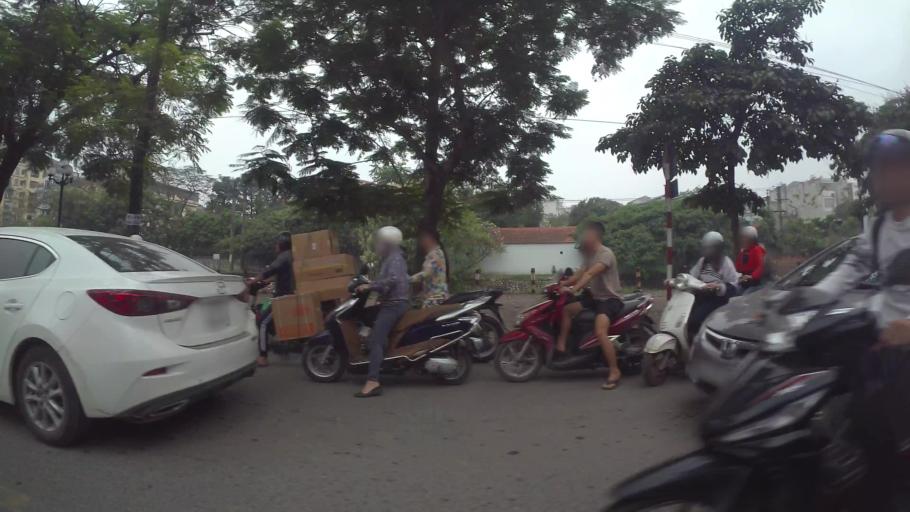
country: VN
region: Ha Noi
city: Hai BaTrung
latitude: 20.9854
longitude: 105.8637
